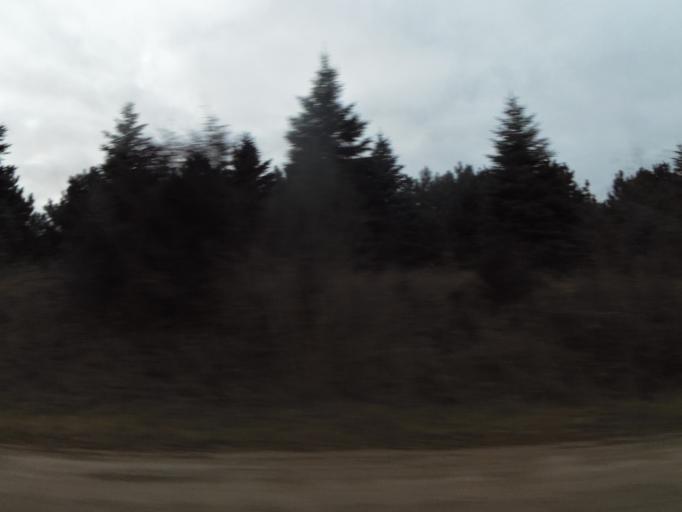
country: US
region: Minnesota
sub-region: Washington County
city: Grant
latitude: 45.0591
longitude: -92.8834
